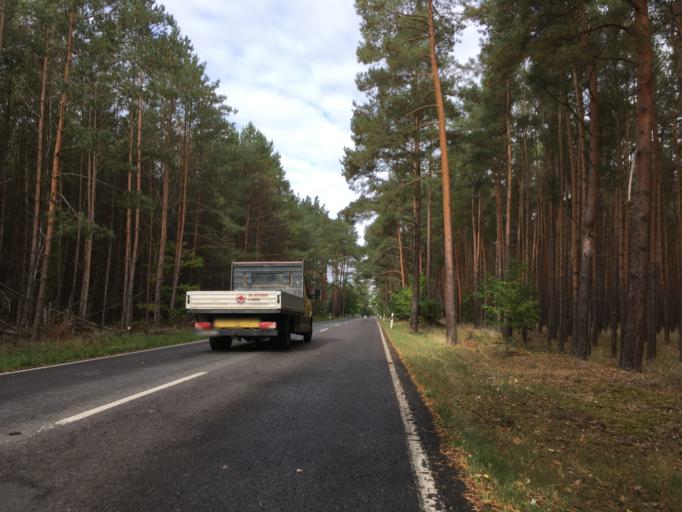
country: PL
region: West Pomeranian Voivodeship
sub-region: Powiat gryfinski
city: Cedynia
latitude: 52.9062
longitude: 14.1242
